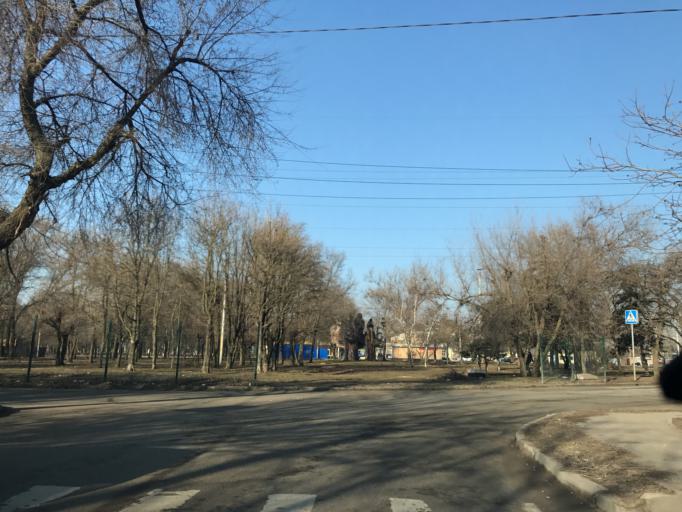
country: RU
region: Rostov
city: Rostov-na-Donu
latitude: 47.2143
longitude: 39.6483
